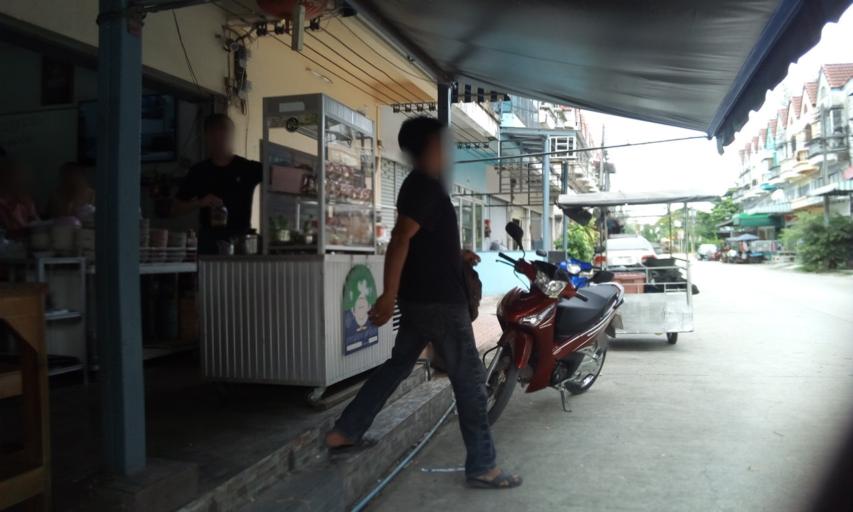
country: TH
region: Pathum Thani
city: Nong Suea
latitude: 14.0667
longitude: 100.8704
